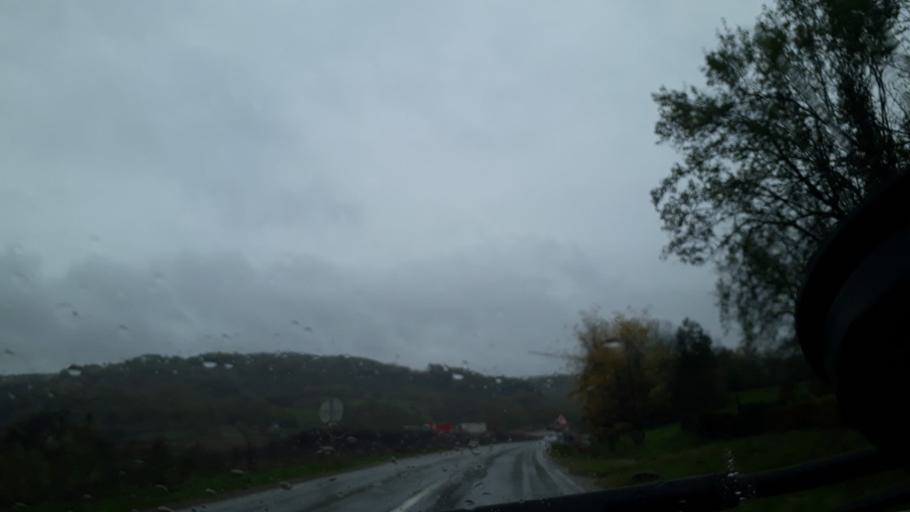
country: BA
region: Republika Srpska
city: Maglajani
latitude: 44.8560
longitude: 17.4556
